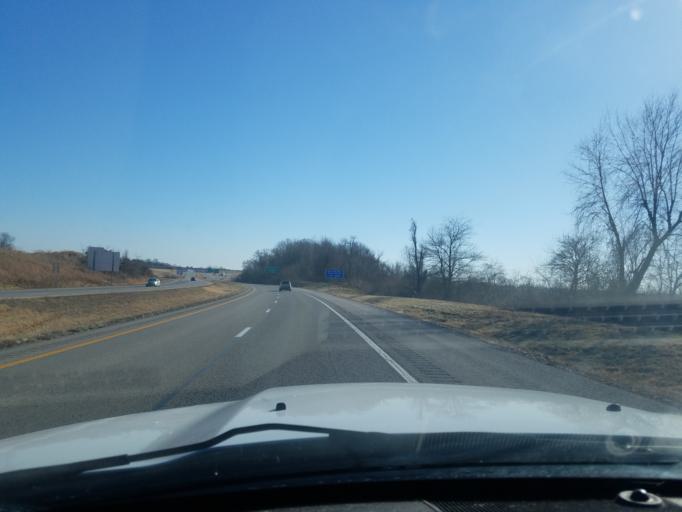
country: US
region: Kentucky
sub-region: Henderson County
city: Henderson
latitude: 37.8046
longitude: -87.5638
